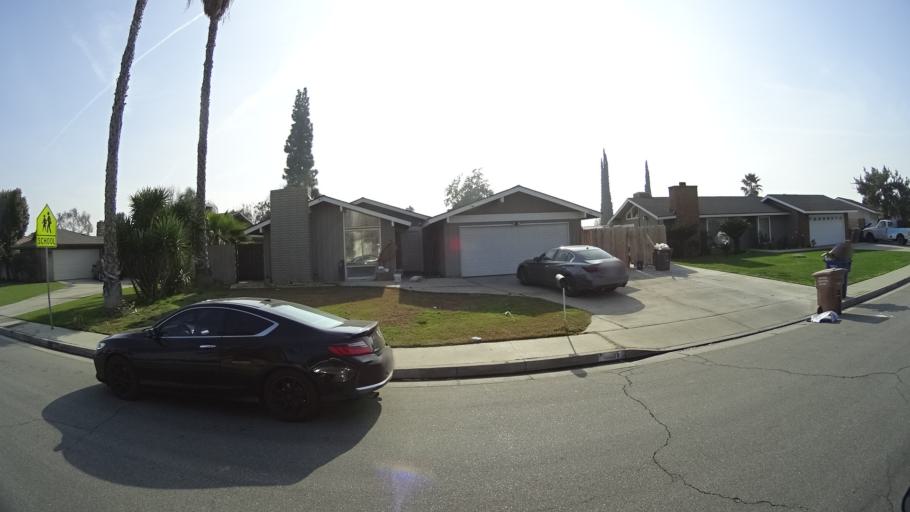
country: US
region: California
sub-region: Kern County
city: Bakersfield
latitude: 35.3656
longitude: -119.0488
